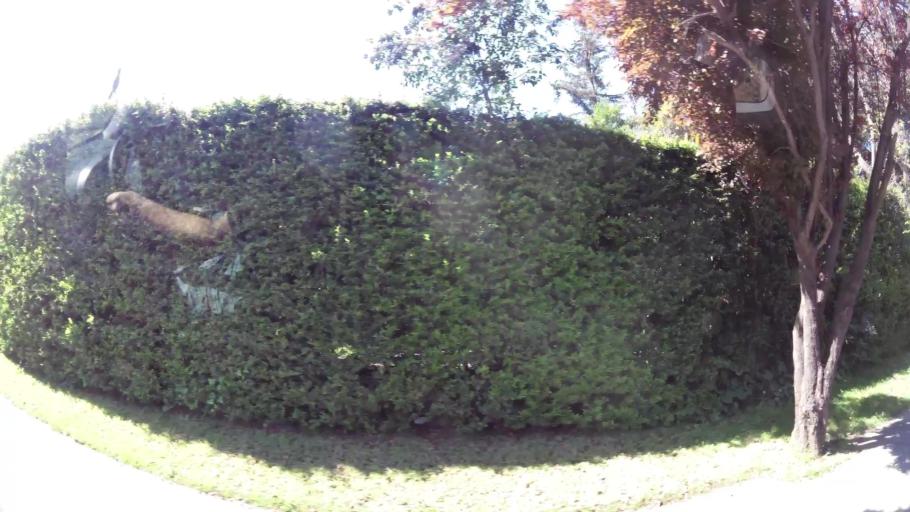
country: CL
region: Santiago Metropolitan
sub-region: Provincia de Santiago
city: Villa Presidente Frei, Nunoa, Santiago, Chile
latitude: -33.4430
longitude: -70.5195
